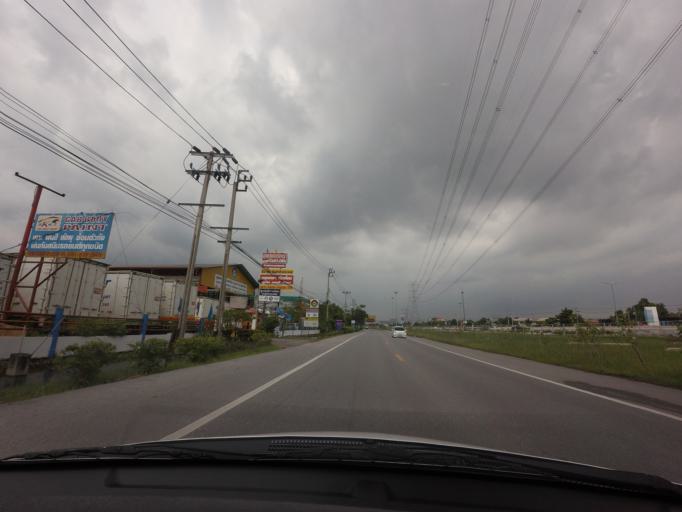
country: TH
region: Bangkok
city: Saphan Sung
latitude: 13.7408
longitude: 100.7020
